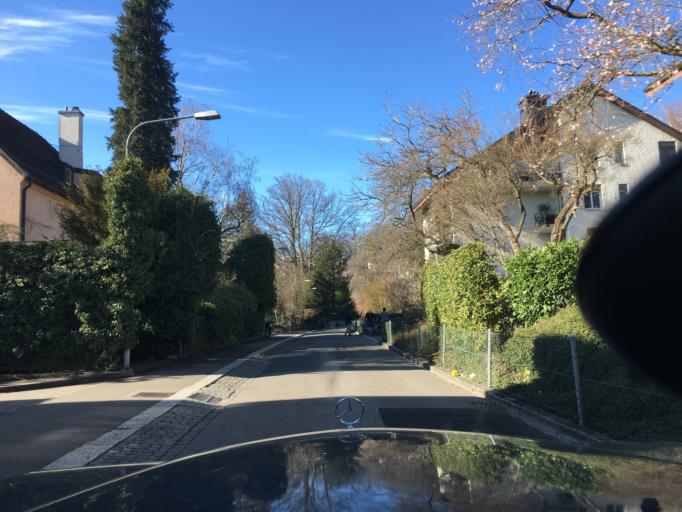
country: CH
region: Zurich
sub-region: Bezirk Zuerich
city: Zuerich (Kreis 7) / Hirslanden
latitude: 47.3637
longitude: 8.5729
